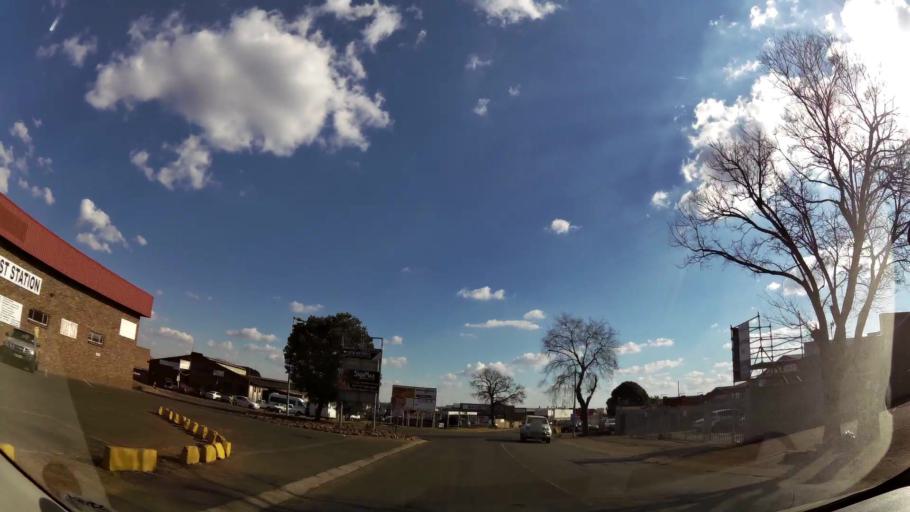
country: ZA
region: Mpumalanga
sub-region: Nkangala District Municipality
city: Witbank
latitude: -25.9023
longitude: 29.2253
